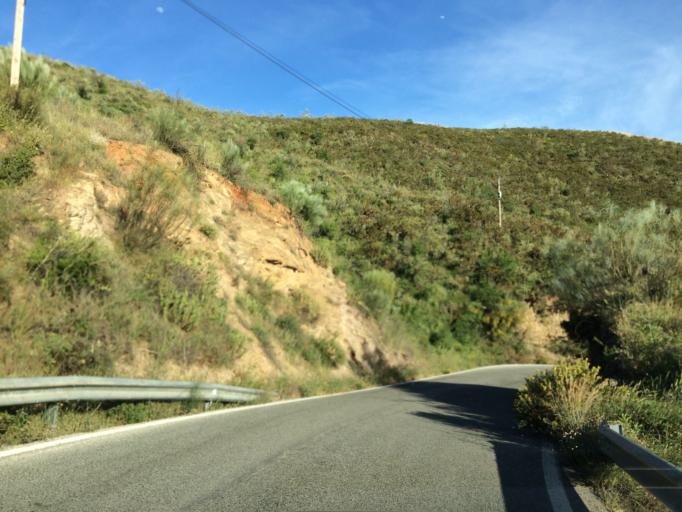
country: ES
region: Andalusia
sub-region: Provincia de Malaga
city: Totalan
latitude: 36.7451
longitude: -4.3295
